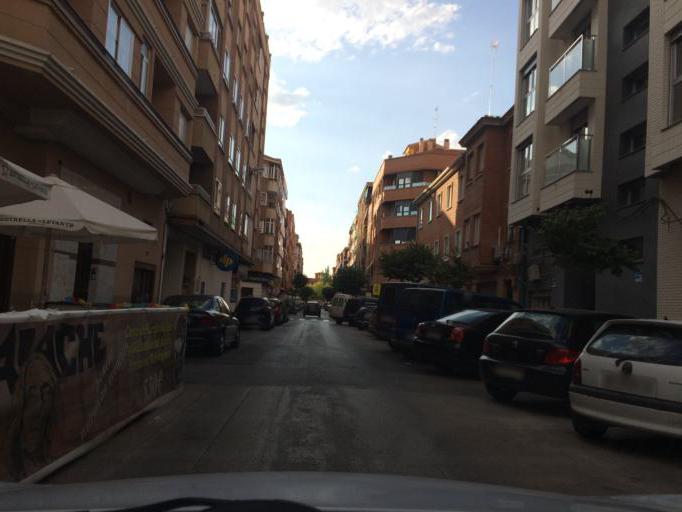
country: ES
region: Castille-La Mancha
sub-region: Provincia de Albacete
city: Albacete
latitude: 38.9907
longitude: -1.8627
